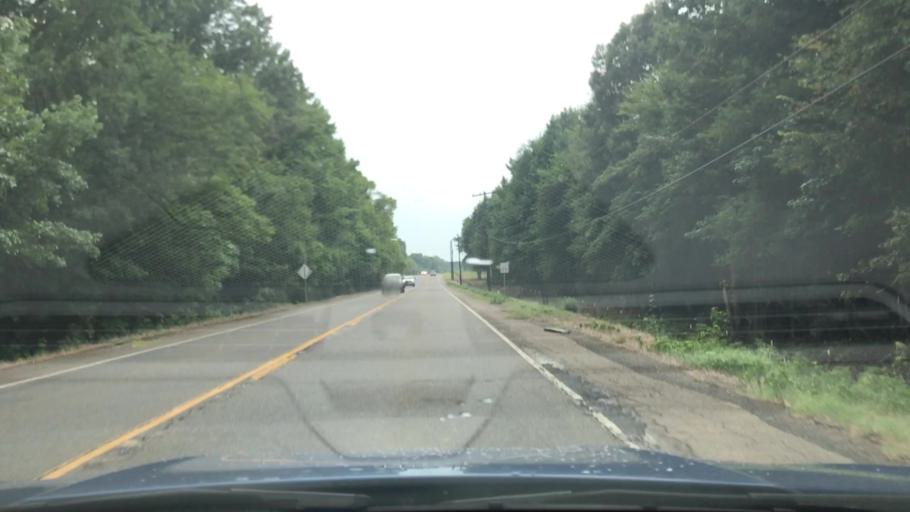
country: US
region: Texas
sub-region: Harrison County
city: Waskom
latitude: 32.4586
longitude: -94.0191
